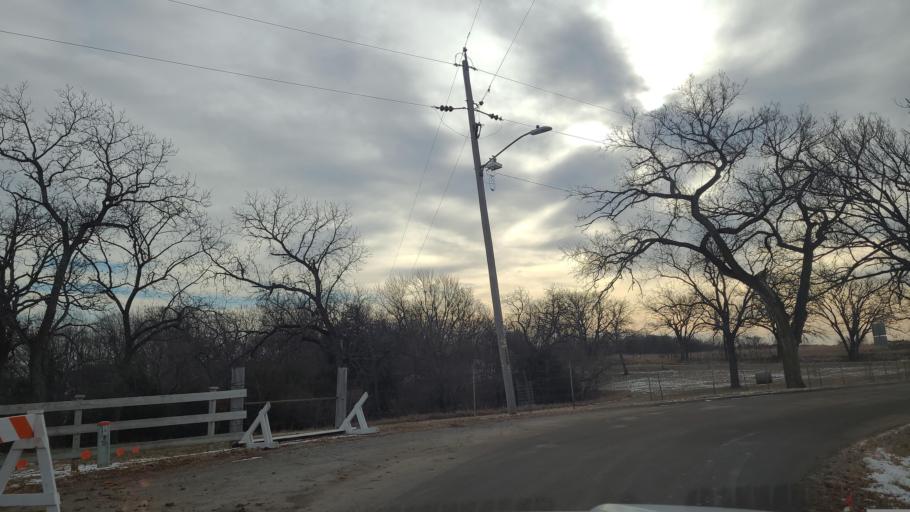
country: US
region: Kansas
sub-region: Douglas County
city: Lawrence
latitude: 39.0378
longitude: -95.3845
